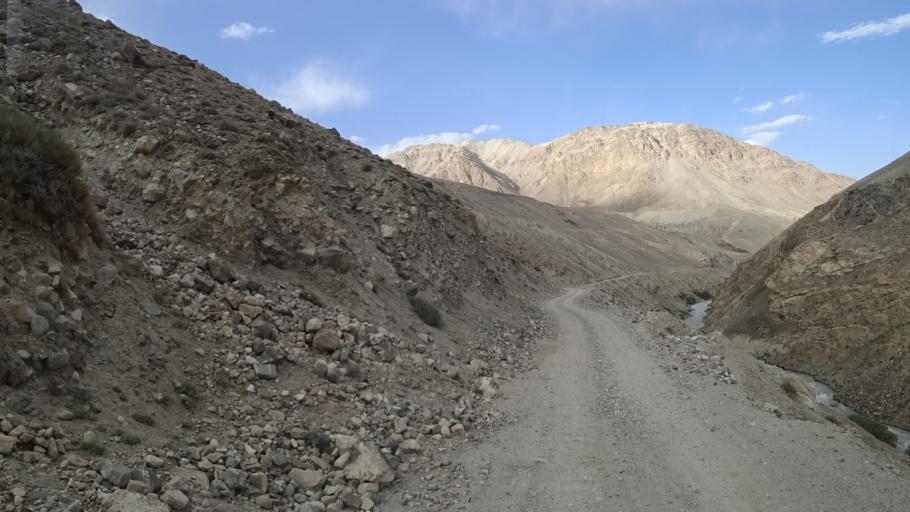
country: AF
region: Badakhshan
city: Khandud
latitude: 37.2299
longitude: 72.8106
